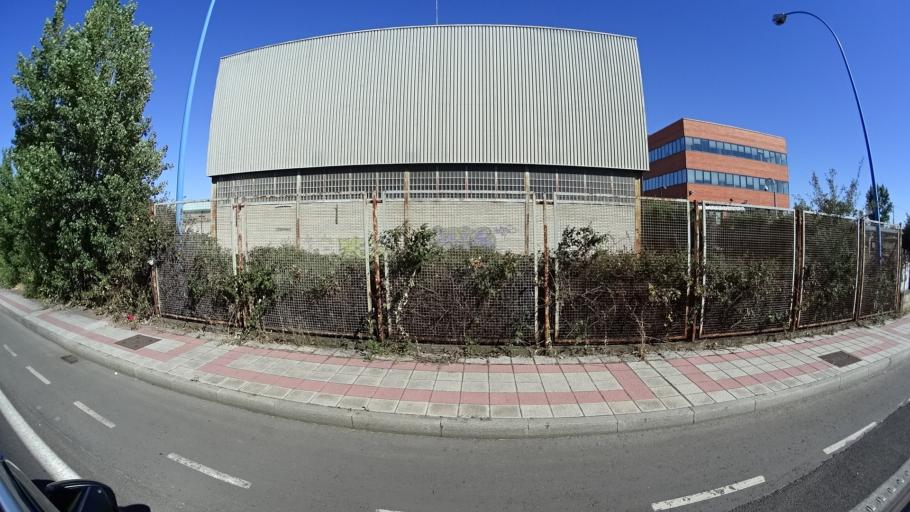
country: ES
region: Castille and Leon
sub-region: Provincia de Leon
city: Leon
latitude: 42.6094
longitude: -5.5561
